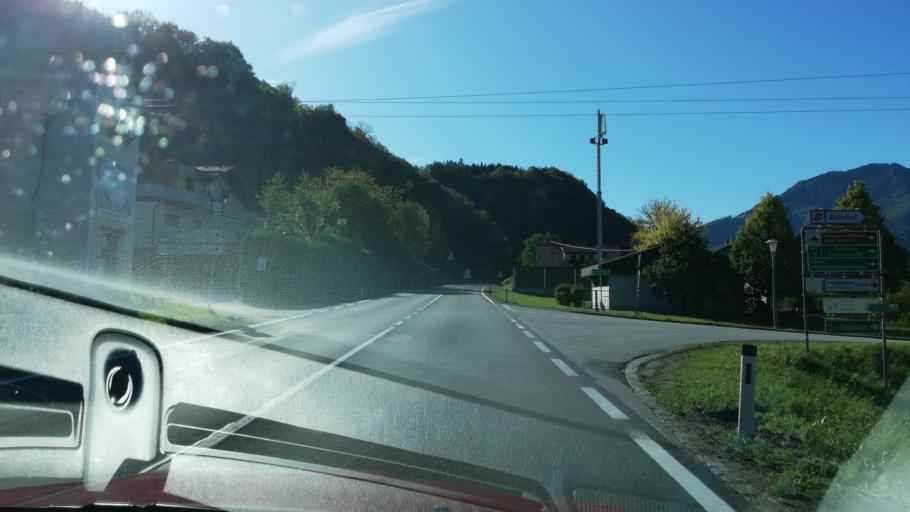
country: AT
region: Upper Austria
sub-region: Politischer Bezirk Steyr-Land
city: Weyer
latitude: 47.8256
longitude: 14.6453
